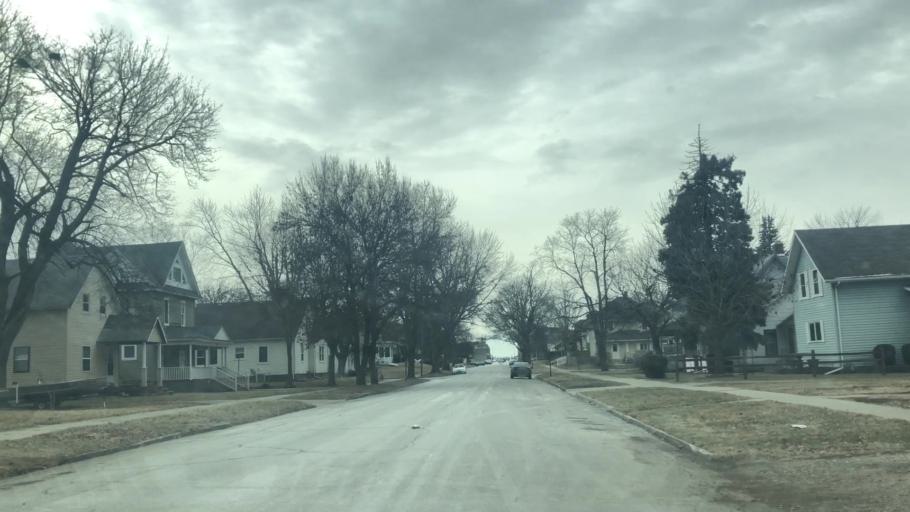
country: US
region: Iowa
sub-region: Marshall County
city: Marshalltown
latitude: 42.0543
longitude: -92.9147
